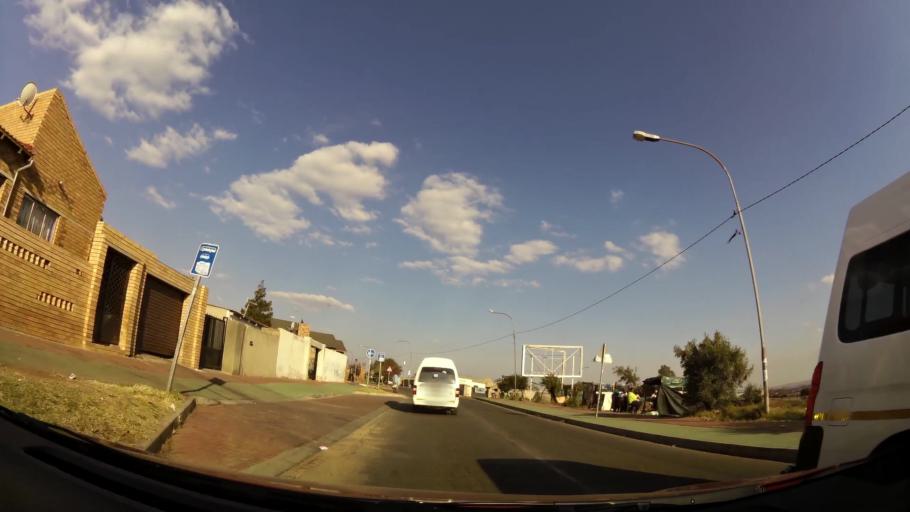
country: ZA
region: Gauteng
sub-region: City of Johannesburg Metropolitan Municipality
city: Soweto
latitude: -26.2182
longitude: 27.8859
